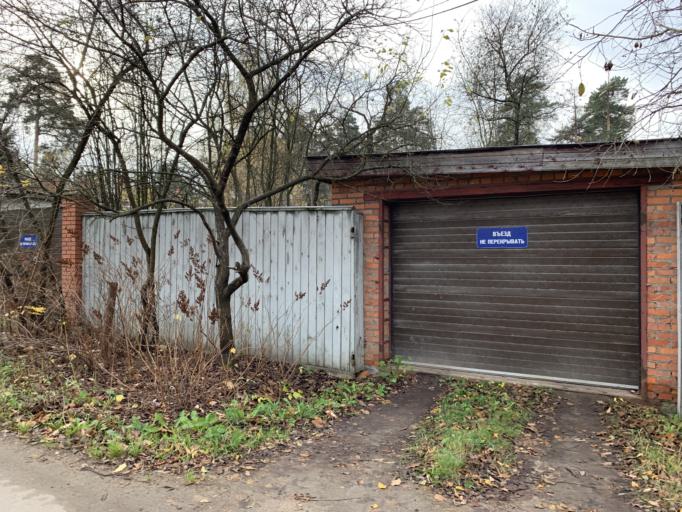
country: RU
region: Moskovskaya
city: Mamontovka
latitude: 55.9872
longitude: 37.8442
